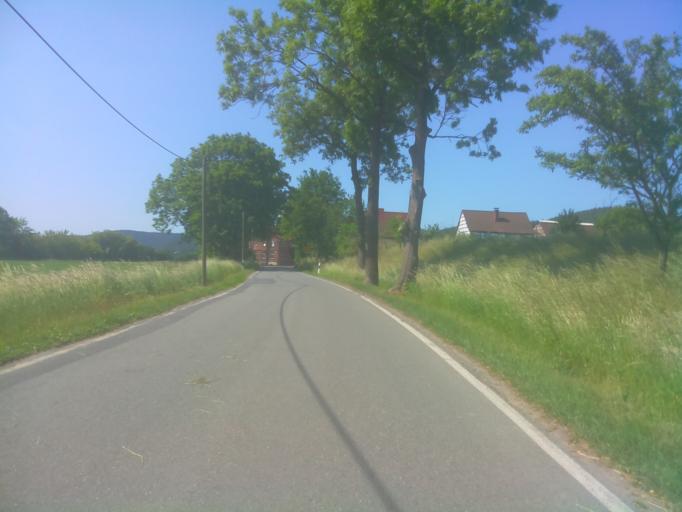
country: DE
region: Thuringia
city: Langenorla
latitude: 50.7192
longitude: 11.6115
